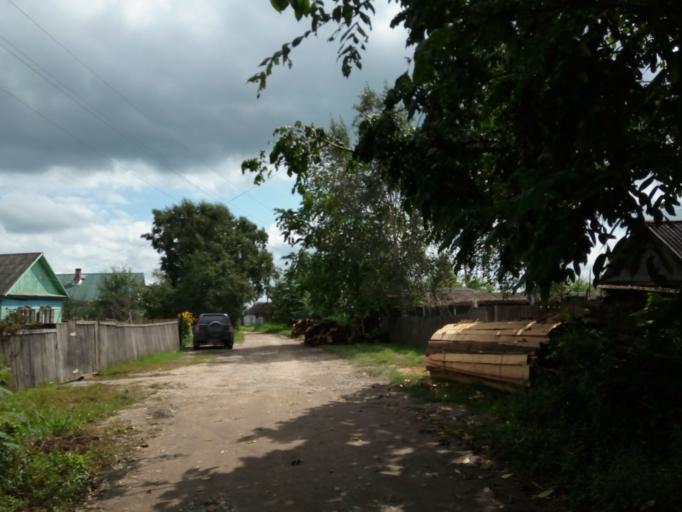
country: RU
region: Primorskiy
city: Dal'nerechensk
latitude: 45.9390
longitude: 133.8139
